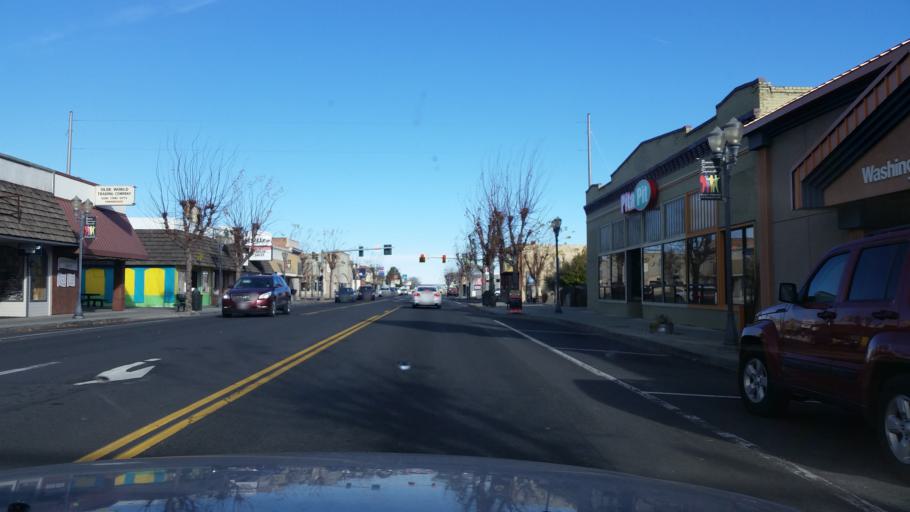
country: US
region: Washington
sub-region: Grant County
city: Ephrata
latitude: 47.3208
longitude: -119.5515
